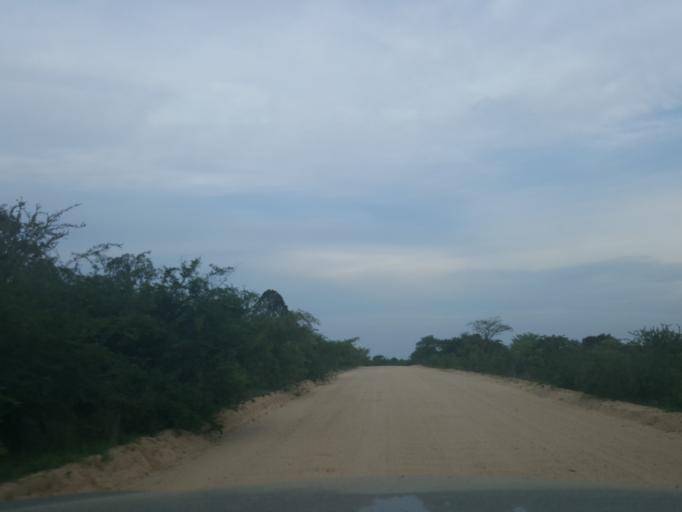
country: ZA
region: Limpopo
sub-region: Mopani District Municipality
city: Hoedspruit
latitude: -24.5642
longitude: 31.0134
